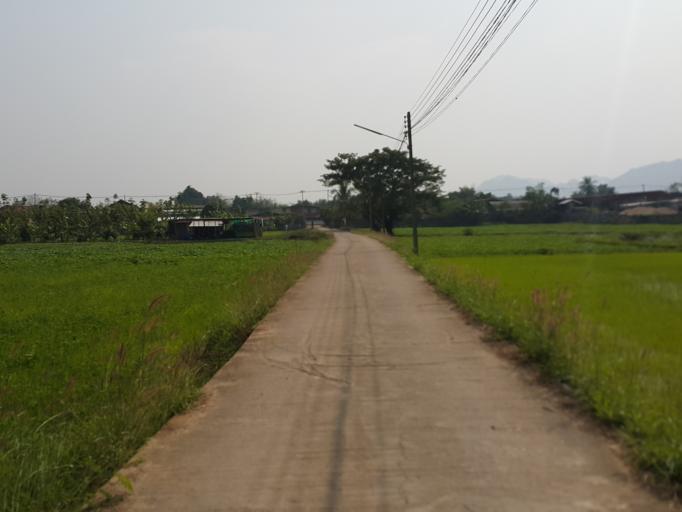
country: TH
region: Sukhothai
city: Thung Saliam
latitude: 17.3299
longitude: 99.5293
